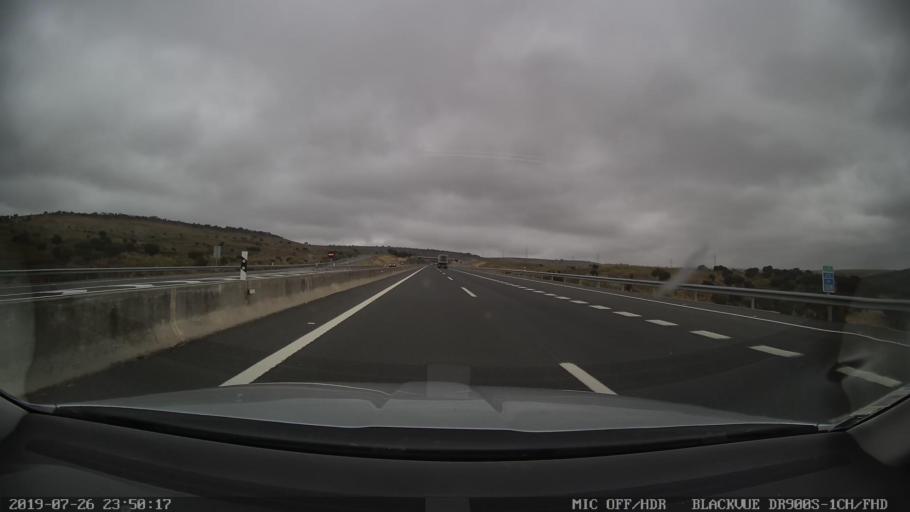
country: ES
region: Extremadura
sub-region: Provincia de Caceres
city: Jaraicejo
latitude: 39.6569
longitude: -5.7995
